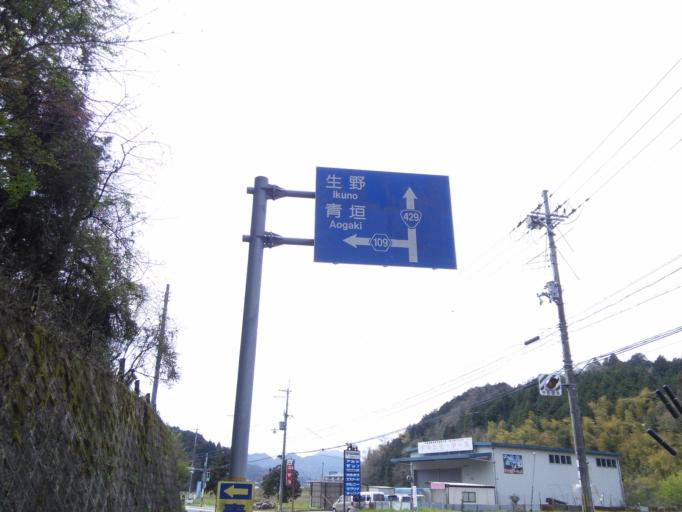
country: JP
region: Kyoto
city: Fukuchiyama
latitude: 35.2893
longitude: 135.0703
